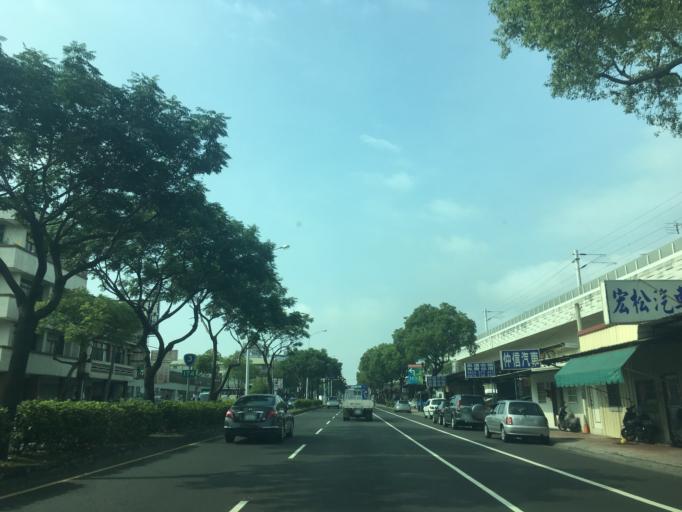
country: TW
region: Taiwan
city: Fengyuan
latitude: 24.2218
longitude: 120.7068
